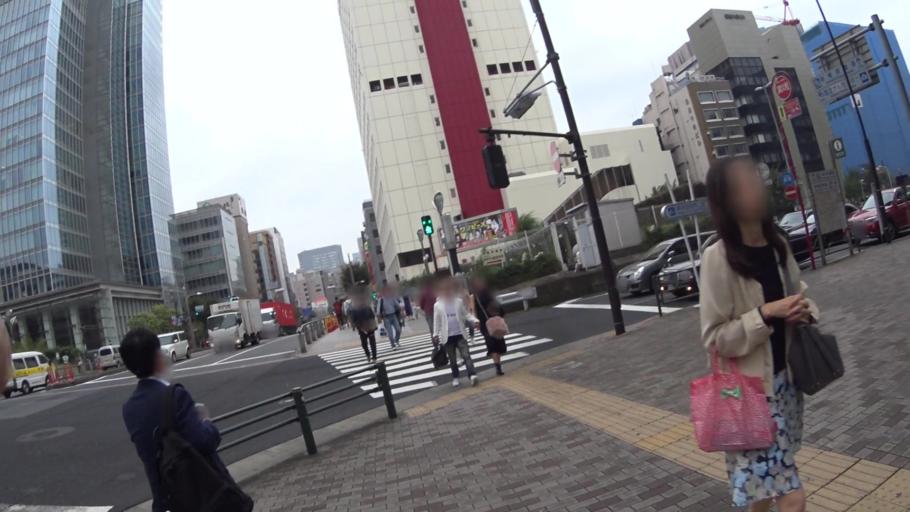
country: JP
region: Tokyo
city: Tokyo
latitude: 35.6687
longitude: 139.7680
